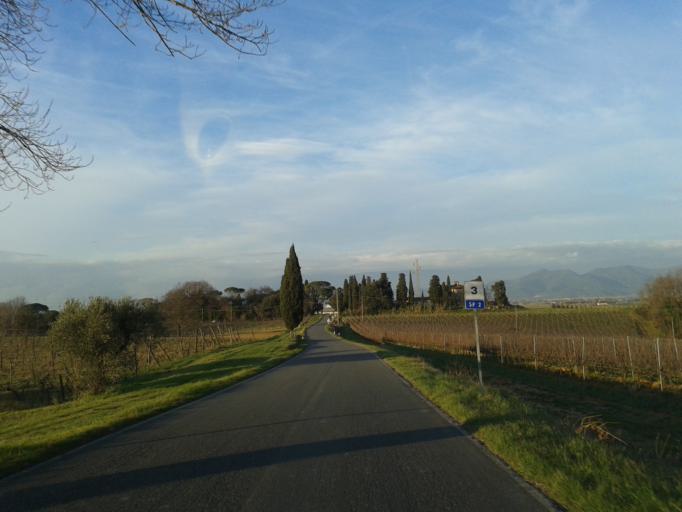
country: IT
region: Tuscany
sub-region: Provincia di Livorno
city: Vicarello
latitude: 43.5939
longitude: 10.4461
